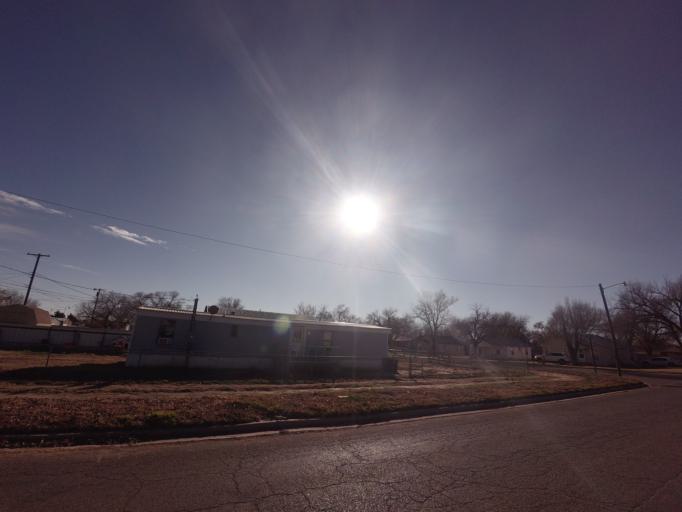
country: US
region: New Mexico
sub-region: Curry County
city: Clovis
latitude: 34.4029
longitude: -103.1823
